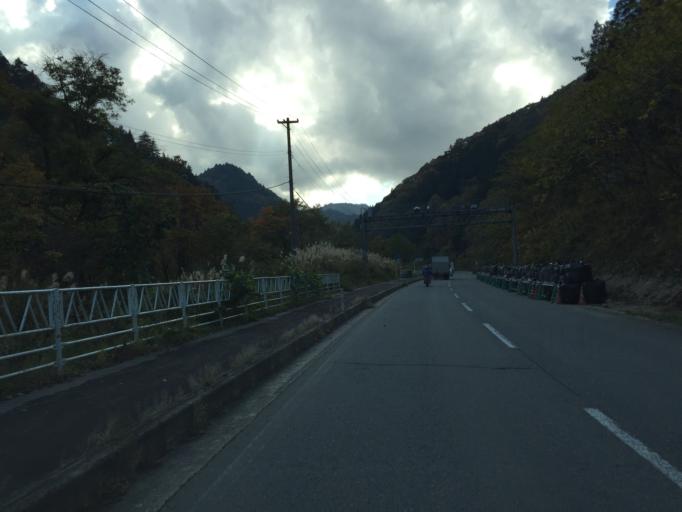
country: JP
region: Yamagata
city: Yonezawa
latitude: 37.8169
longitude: 140.0005
